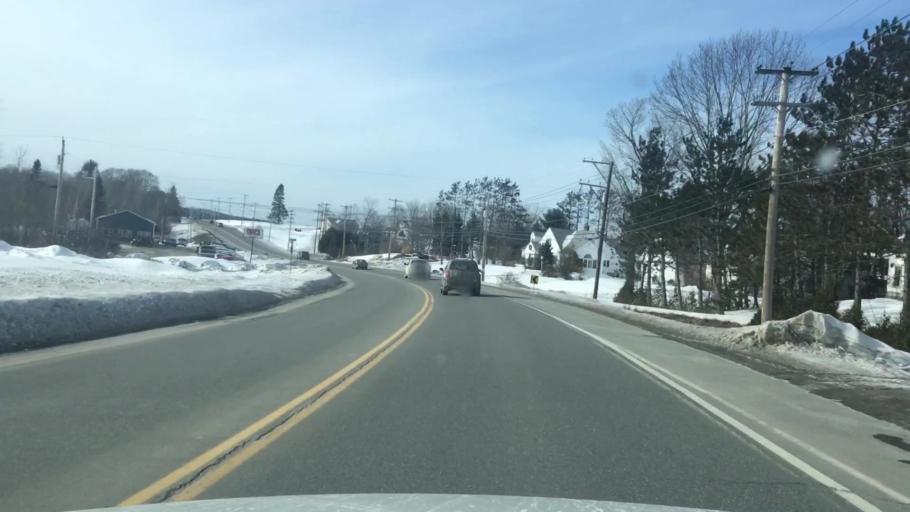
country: US
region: Maine
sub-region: Penobscot County
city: Bangor
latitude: 44.8516
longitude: -68.8063
